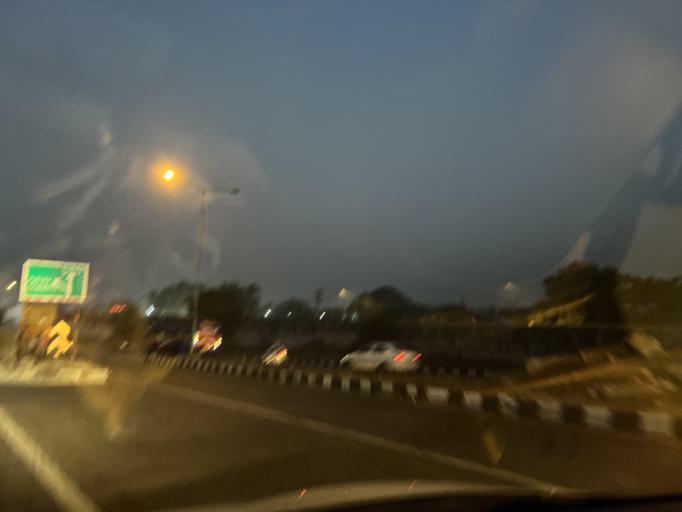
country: IN
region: Odisha
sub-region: Cuttack
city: Cuttack
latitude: 20.4445
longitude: 85.8948
